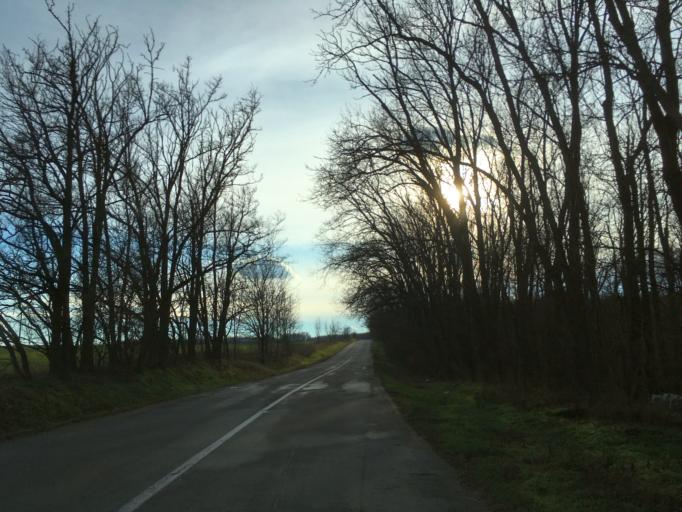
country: SK
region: Nitriansky
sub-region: Okres Nove Zamky
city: Nove Zamky
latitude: 47.9576
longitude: 18.2510
